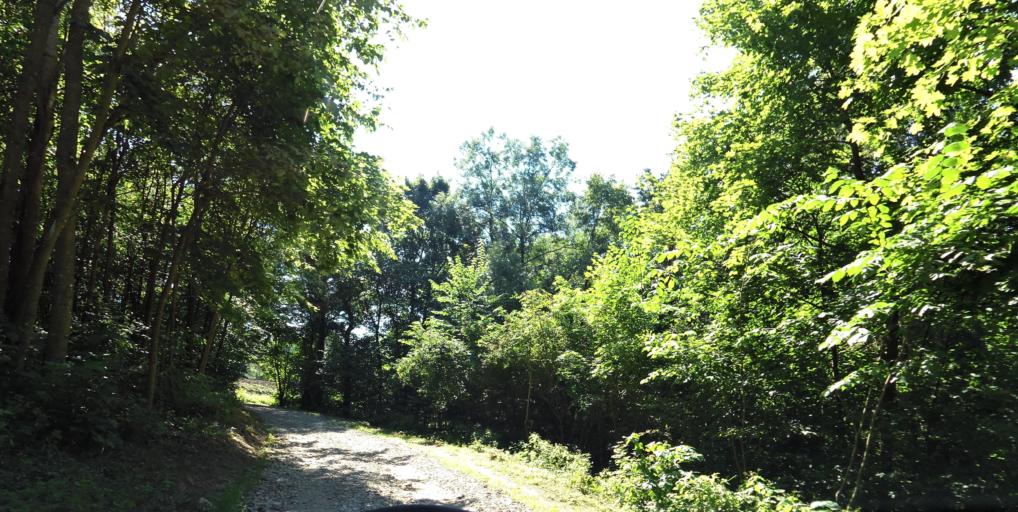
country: LT
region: Vilnius County
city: Rasos
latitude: 54.6820
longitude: 25.3619
